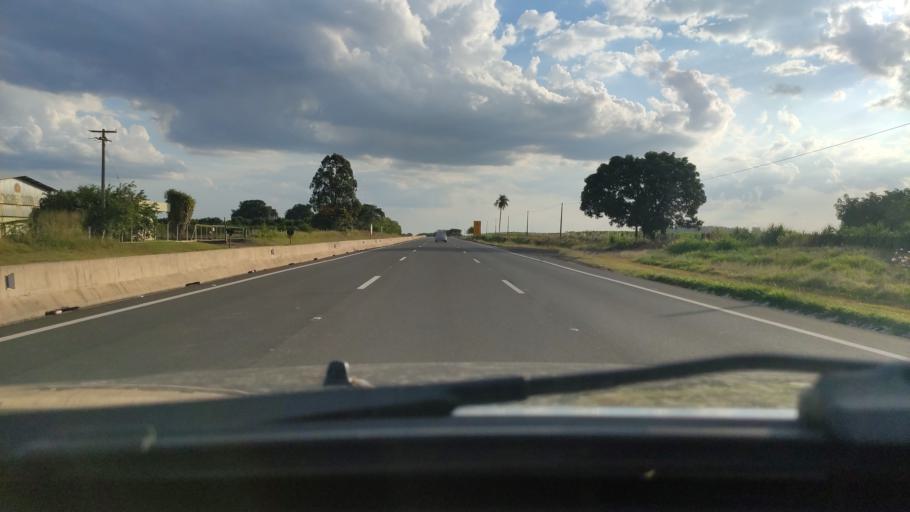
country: BR
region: Sao Paulo
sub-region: Mogi-Mirim
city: Mogi Mirim
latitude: -22.4551
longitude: -47.0919
